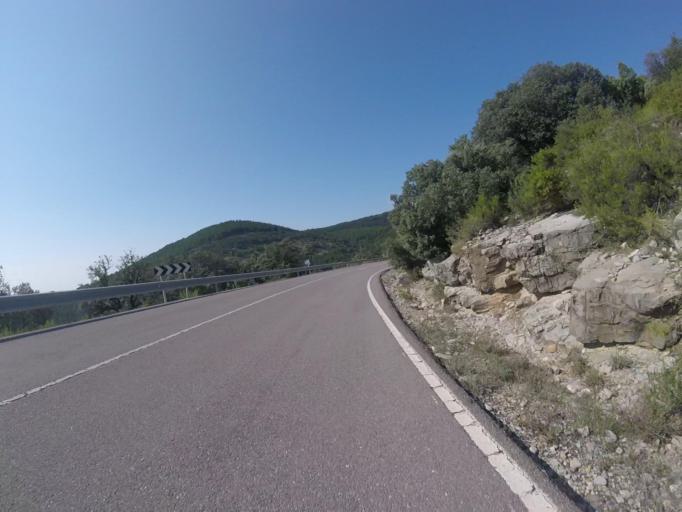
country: ES
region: Valencia
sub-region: Provincia de Castello
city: Benafigos
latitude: 40.2706
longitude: -0.2403
